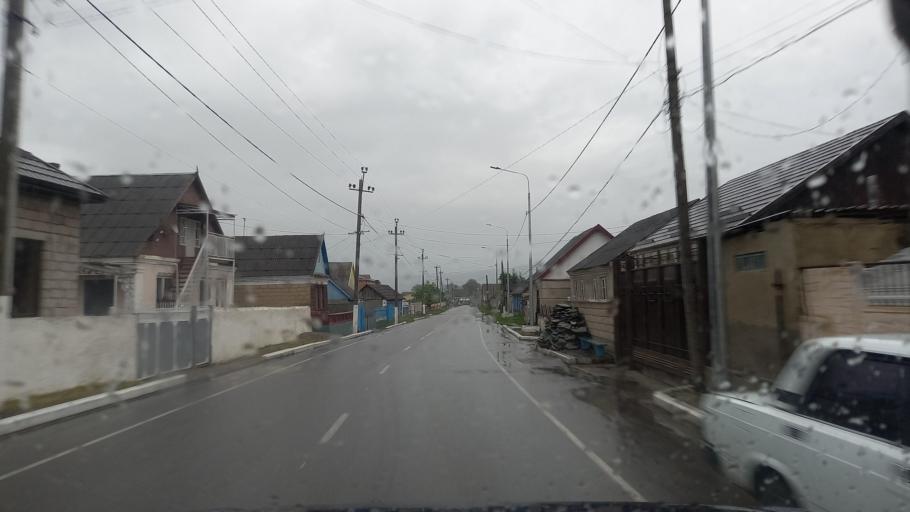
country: RU
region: Kabardino-Balkariya
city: Gundelen
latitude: 43.5958
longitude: 43.1648
